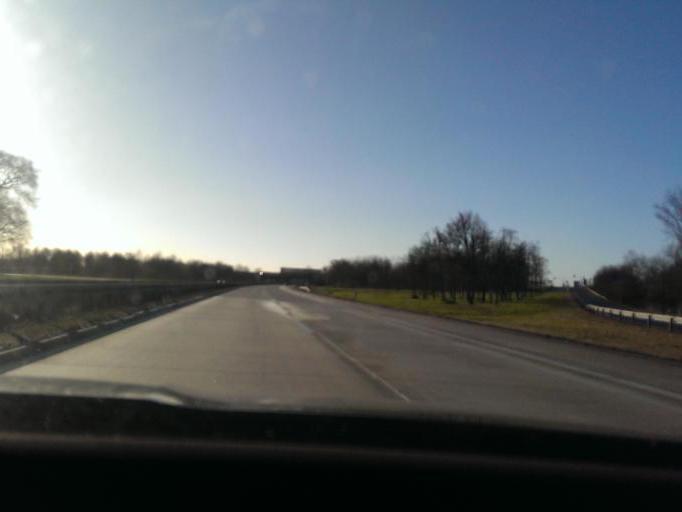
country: DE
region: Lower Saxony
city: Langenhagen
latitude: 52.4623
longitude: 9.7225
